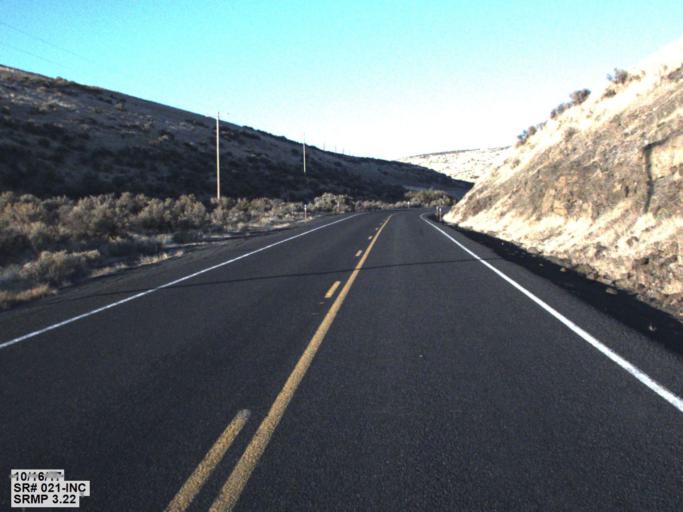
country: US
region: Washington
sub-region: Franklin County
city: Connell
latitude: 46.6850
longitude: -118.5343
